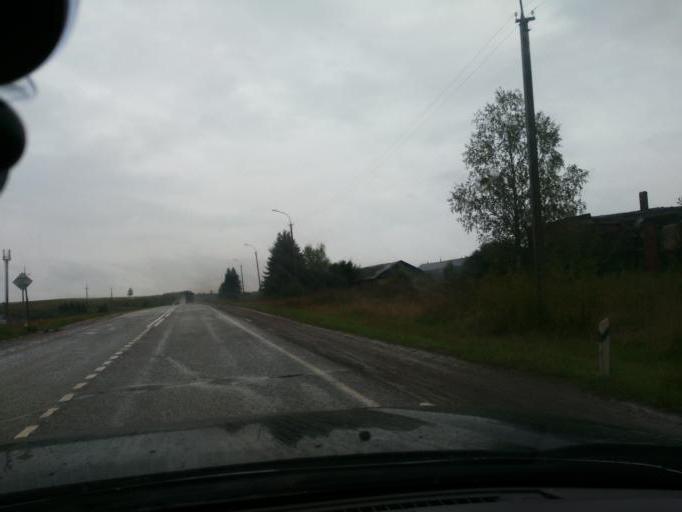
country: RU
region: Perm
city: Yugo-Kamskiy
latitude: 57.4596
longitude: 55.6648
